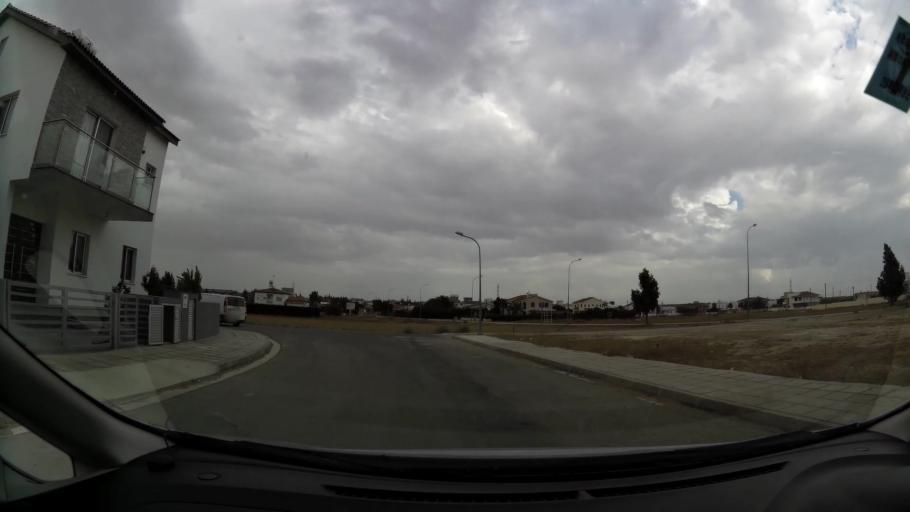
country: CY
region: Lefkosia
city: Geri
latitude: 35.1063
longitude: 33.3936
